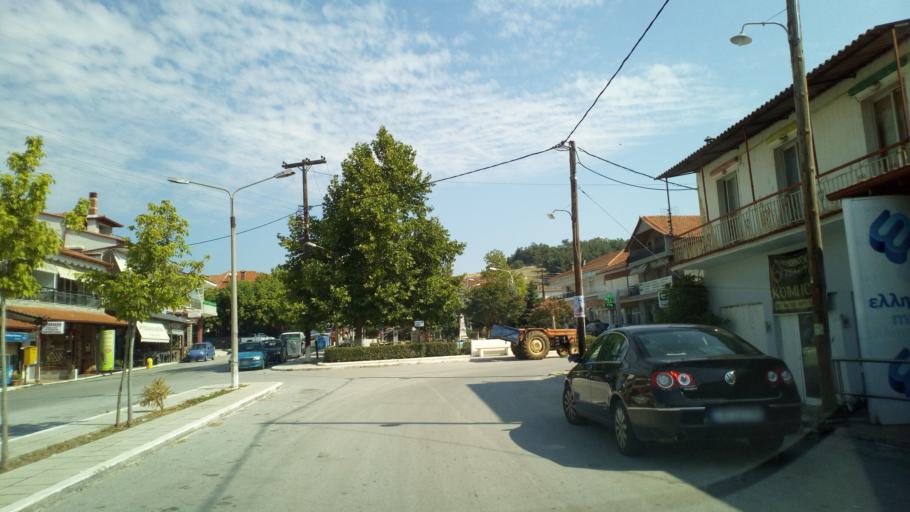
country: GR
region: Central Macedonia
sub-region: Nomos Thessalonikis
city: Askos
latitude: 40.7505
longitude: 23.3873
